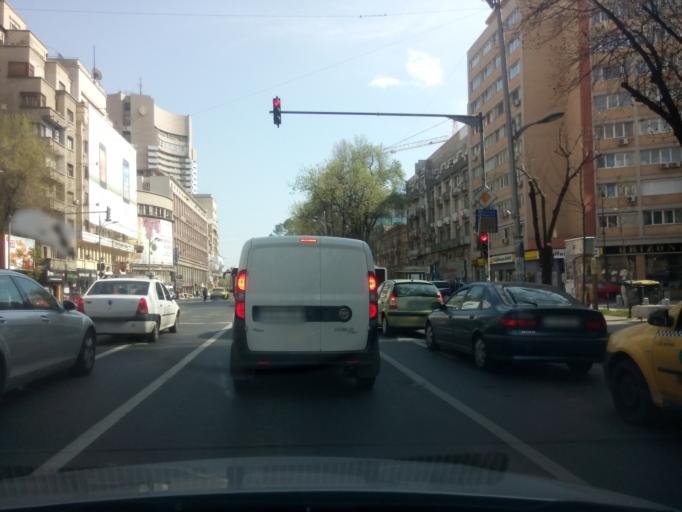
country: RO
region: Bucuresti
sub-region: Municipiul Bucuresti
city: Bucharest
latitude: 44.4395
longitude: 26.1003
